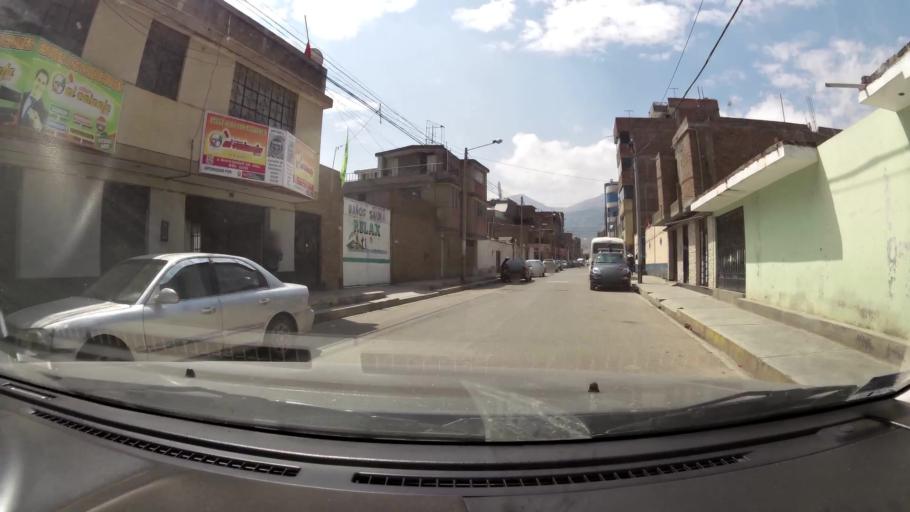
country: PE
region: Junin
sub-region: Provincia de Huancayo
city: Huancayo
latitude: -12.0833
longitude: -75.2059
